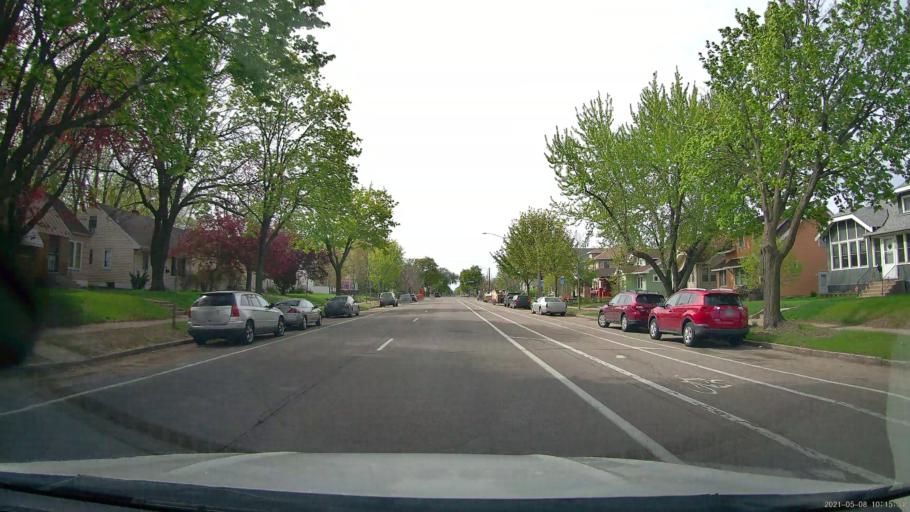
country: US
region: Minnesota
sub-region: Hennepin County
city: Richfield
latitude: 44.9284
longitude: -93.2675
